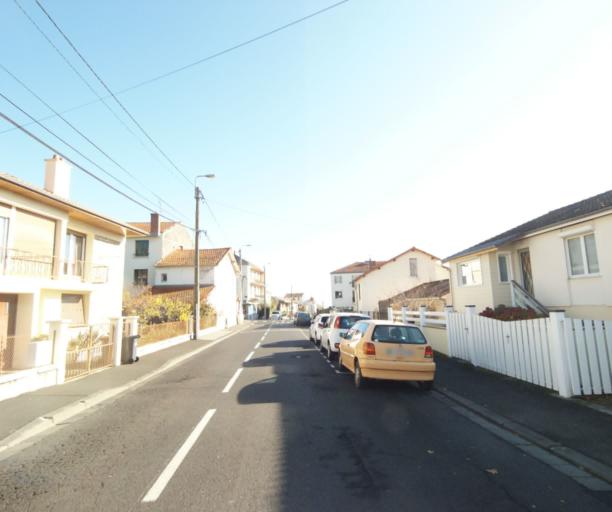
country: FR
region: Auvergne
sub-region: Departement du Puy-de-Dome
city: Clermont-Ferrand
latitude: 45.7935
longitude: 3.0819
